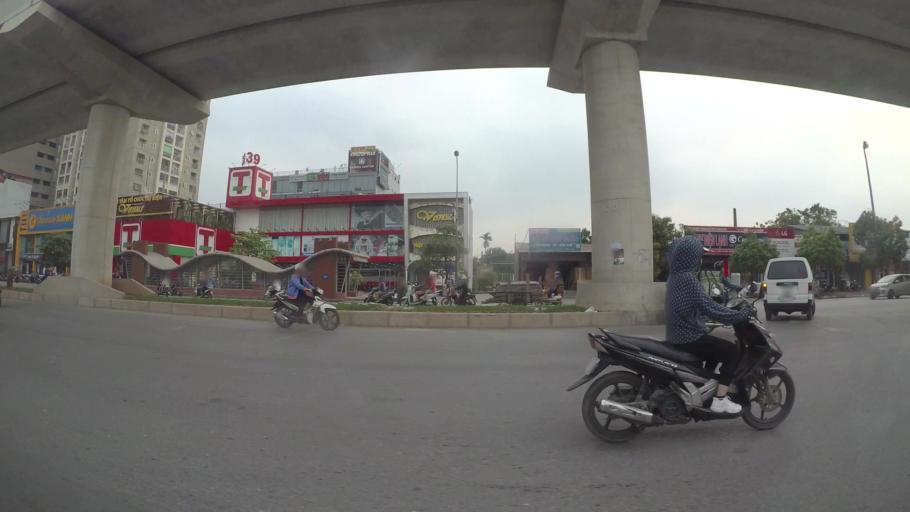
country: VN
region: Ha Noi
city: Cau Dien
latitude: 21.0429
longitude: 105.7582
